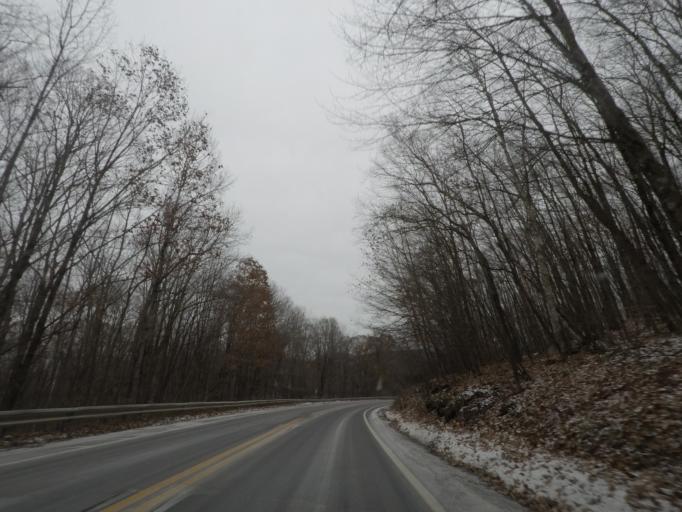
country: US
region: Massachusetts
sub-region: Berkshire County
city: Williamstown
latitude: 42.7045
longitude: -73.2414
